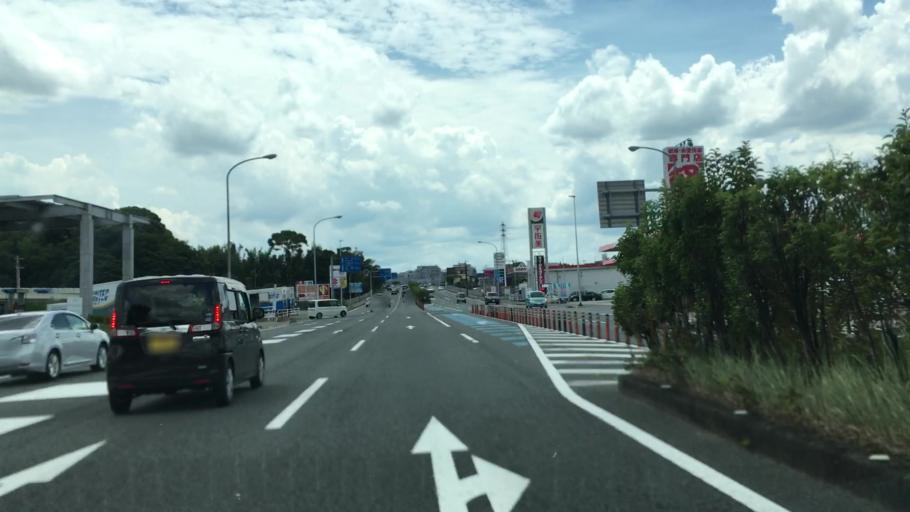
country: JP
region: Fukuoka
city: Chikushino-shi
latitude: 33.4797
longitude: 130.5389
